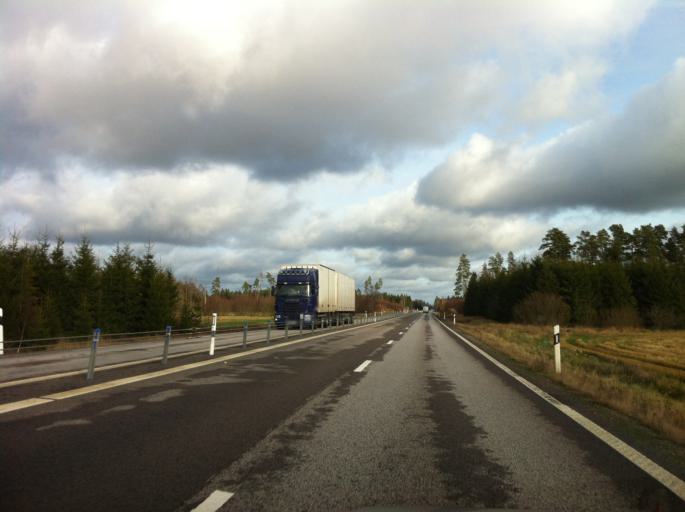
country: SE
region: Kronoberg
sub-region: Alvesta Kommun
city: Vislanda
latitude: 56.7155
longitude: 14.4500
